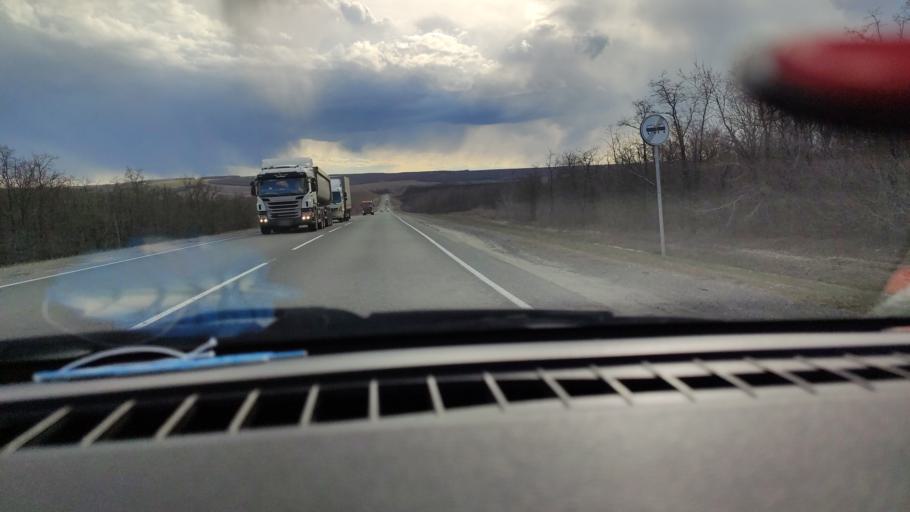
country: RU
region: Saratov
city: Sinodskoye
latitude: 51.9315
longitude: 46.5805
